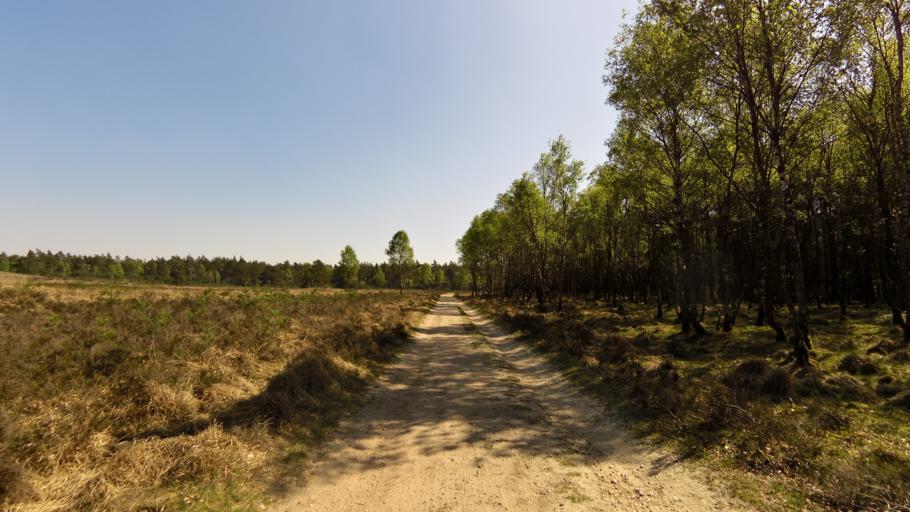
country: NL
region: Gelderland
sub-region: Gemeente Rozendaal
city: Rozendaal
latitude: 52.0313
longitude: 5.9419
